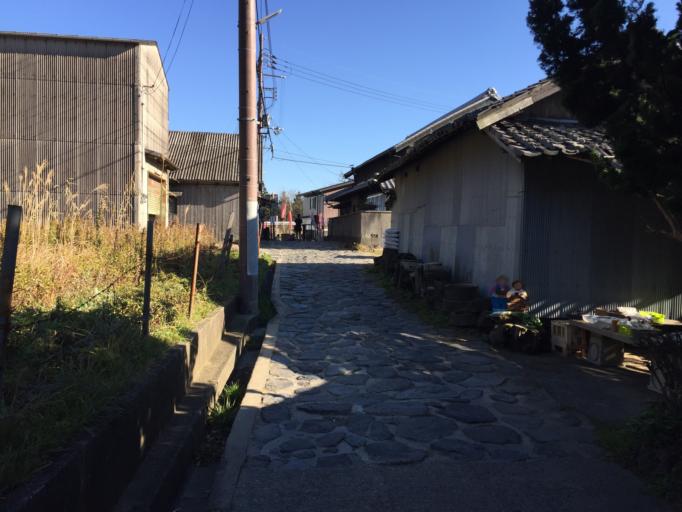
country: JP
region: Nara
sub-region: Ikoma-shi
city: Ikoma
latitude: 34.6659
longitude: 135.6708
